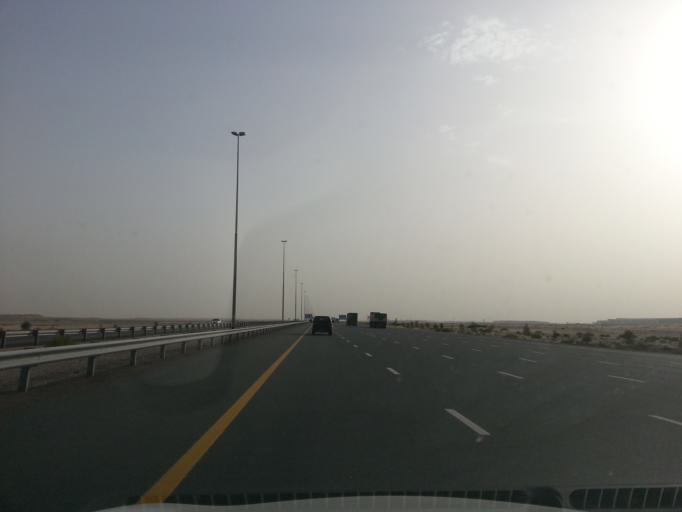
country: AE
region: Dubai
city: Dubai
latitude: 24.8237
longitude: 55.1250
